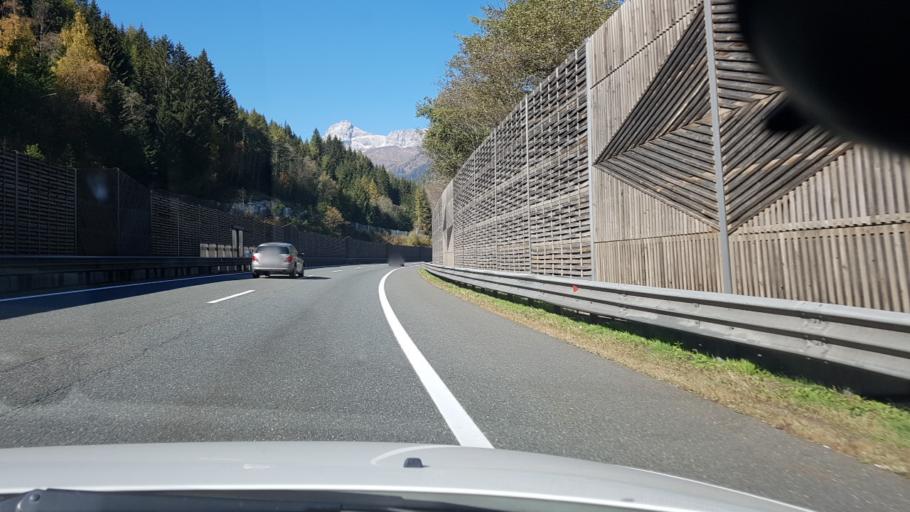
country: AT
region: Salzburg
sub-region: Politischer Bezirk Tamsweg
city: Zederhaus
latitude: 47.1648
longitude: 13.4681
